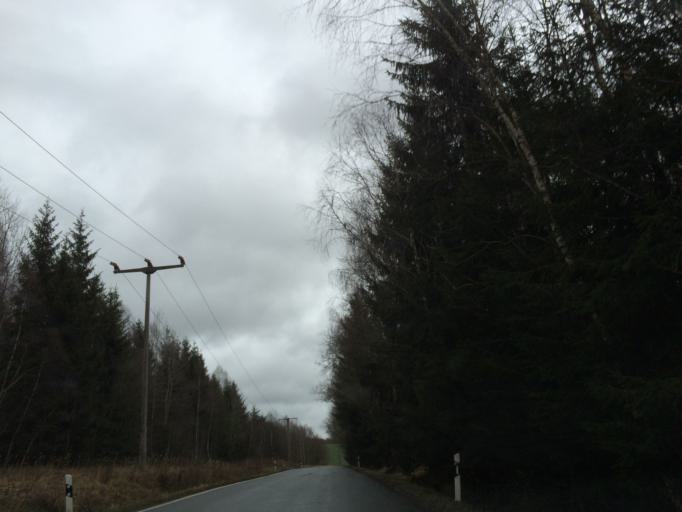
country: DE
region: Thuringia
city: Dreba
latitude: 50.6788
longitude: 11.7327
